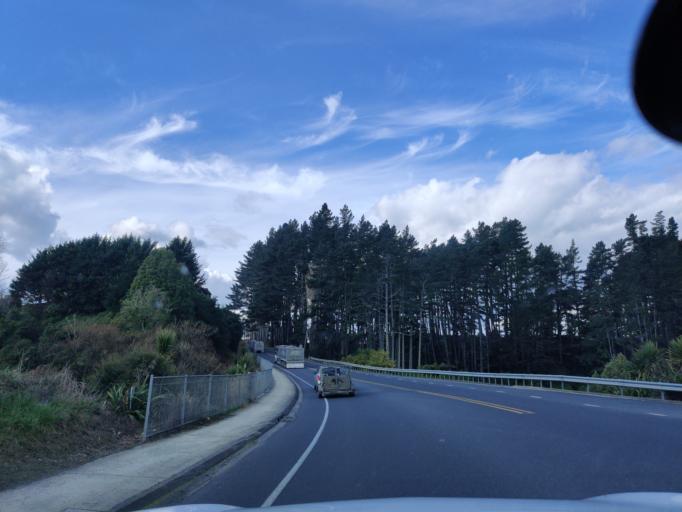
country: NZ
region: Waikato
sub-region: Hamilton City
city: Hamilton
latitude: -37.8273
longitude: 175.3606
